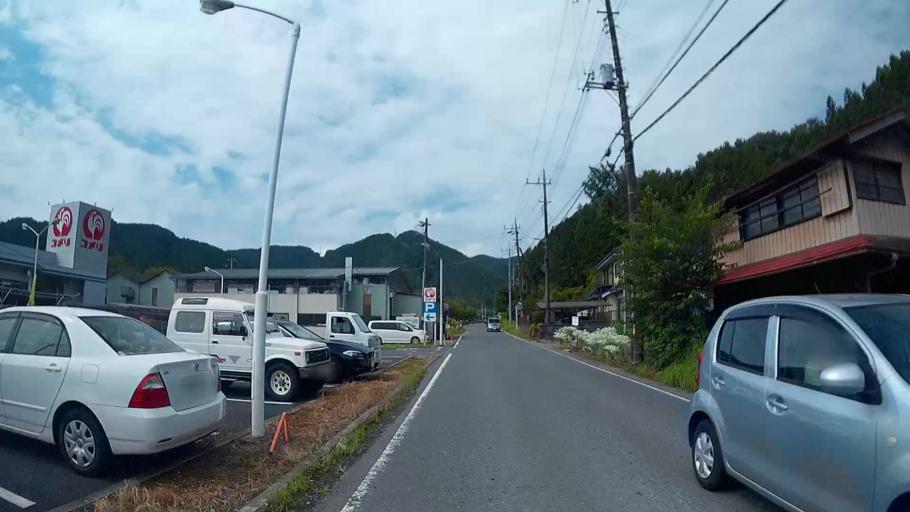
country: JP
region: Saitama
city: Hanno
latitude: 35.8687
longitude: 139.2591
